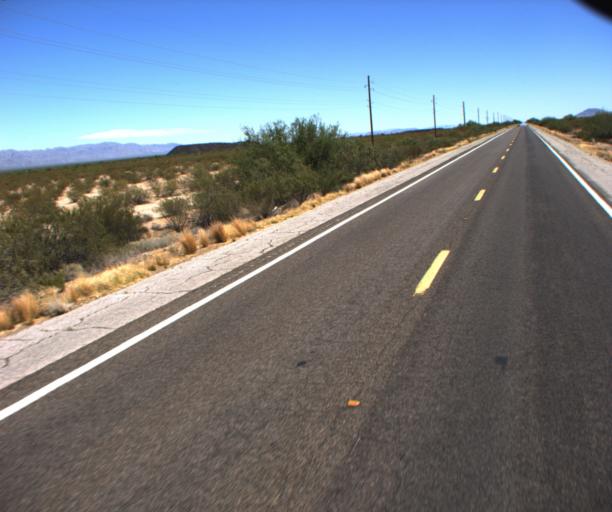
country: US
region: Arizona
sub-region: La Paz County
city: Salome
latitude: 33.8257
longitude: -113.5215
